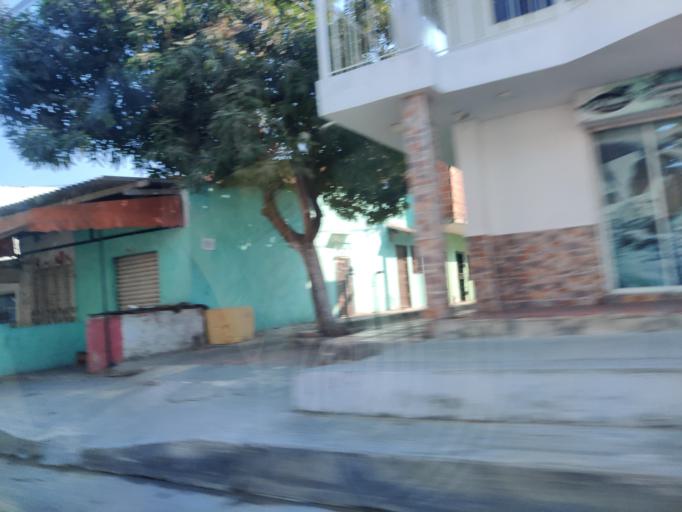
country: CO
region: Atlantico
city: Soledad
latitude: 10.9109
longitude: -74.8010
